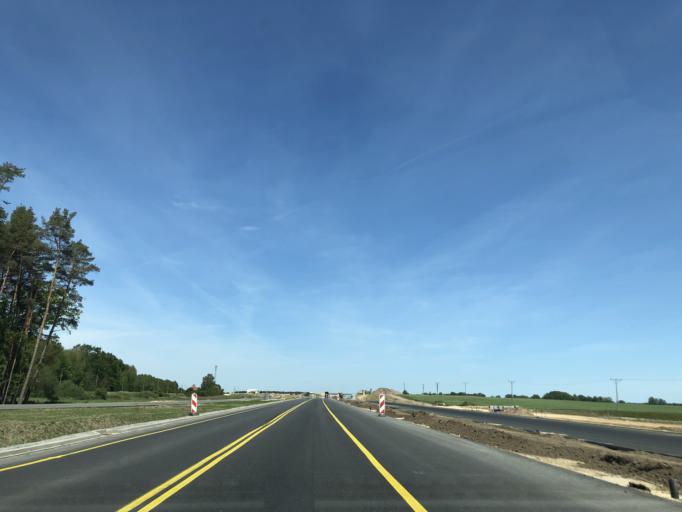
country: PL
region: West Pomeranian Voivodeship
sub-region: Powiat gryficki
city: Ploty
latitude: 53.7373
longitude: 15.2072
